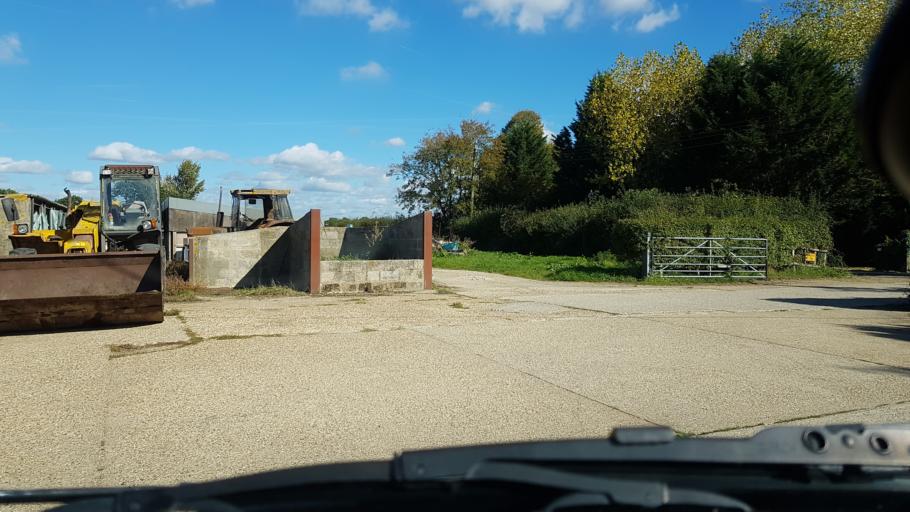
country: GB
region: England
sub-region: West Sussex
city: Billingshurst
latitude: 50.9936
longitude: -0.4356
